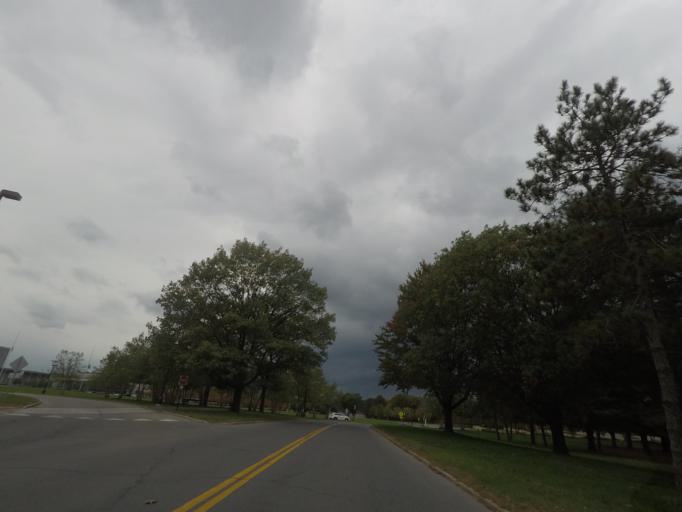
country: US
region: New York
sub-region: Albany County
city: Roessleville
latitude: 42.6883
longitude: -73.8195
